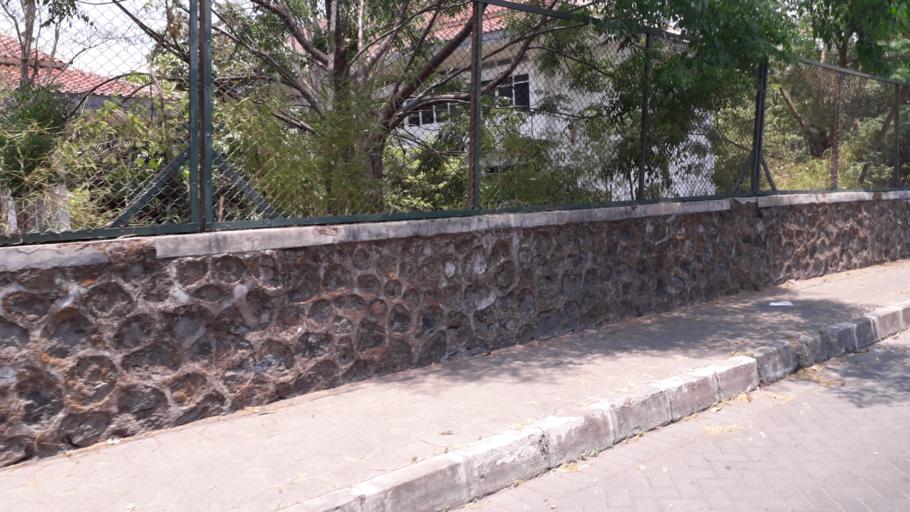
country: ID
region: Daerah Istimewa Yogyakarta
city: Yogyakarta
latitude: -7.7637
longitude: 110.3733
